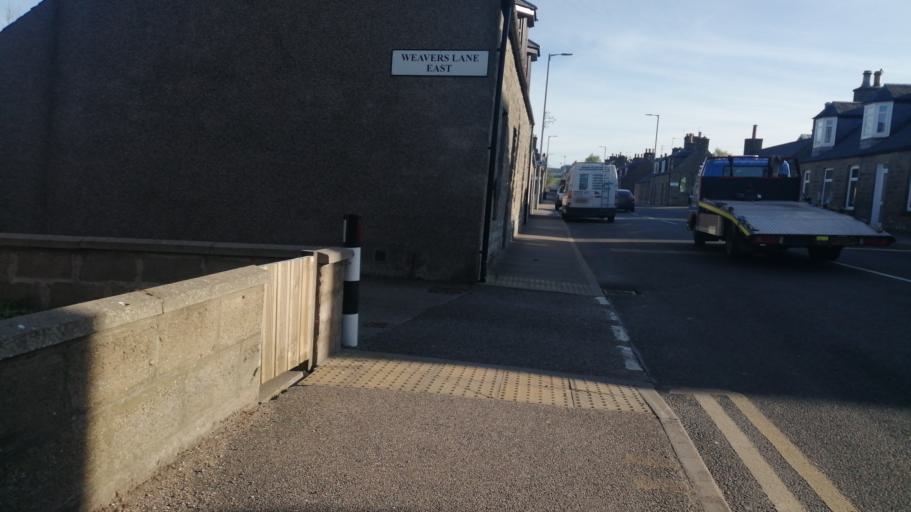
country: GB
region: Scotland
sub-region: Moray
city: Keith
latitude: 57.5414
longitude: -2.9481
